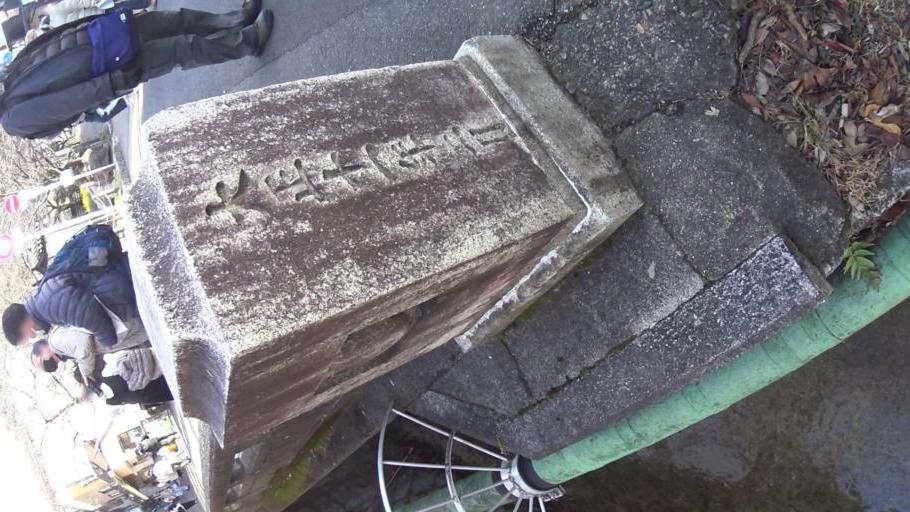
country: JP
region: Kyoto
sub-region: Kyoto-shi
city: Kamigyo-ku
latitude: 35.0247
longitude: 135.8009
